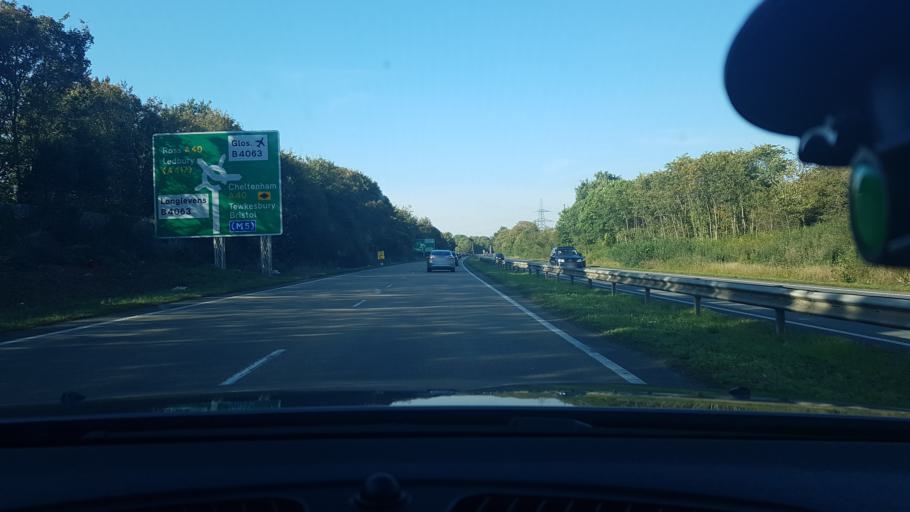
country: GB
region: England
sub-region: Gloucestershire
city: Barnwood
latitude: 51.8736
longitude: -2.1989
